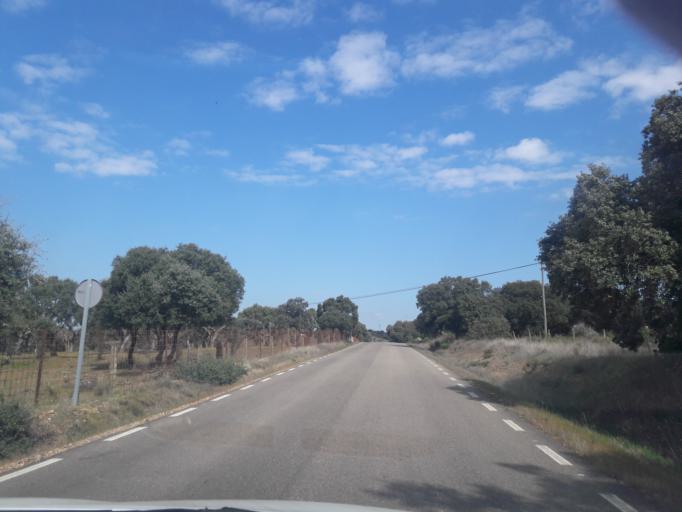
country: ES
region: Castille and Leon
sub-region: Provincia de Salamanca
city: Zamarra
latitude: 40.5627
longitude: -6.4725
